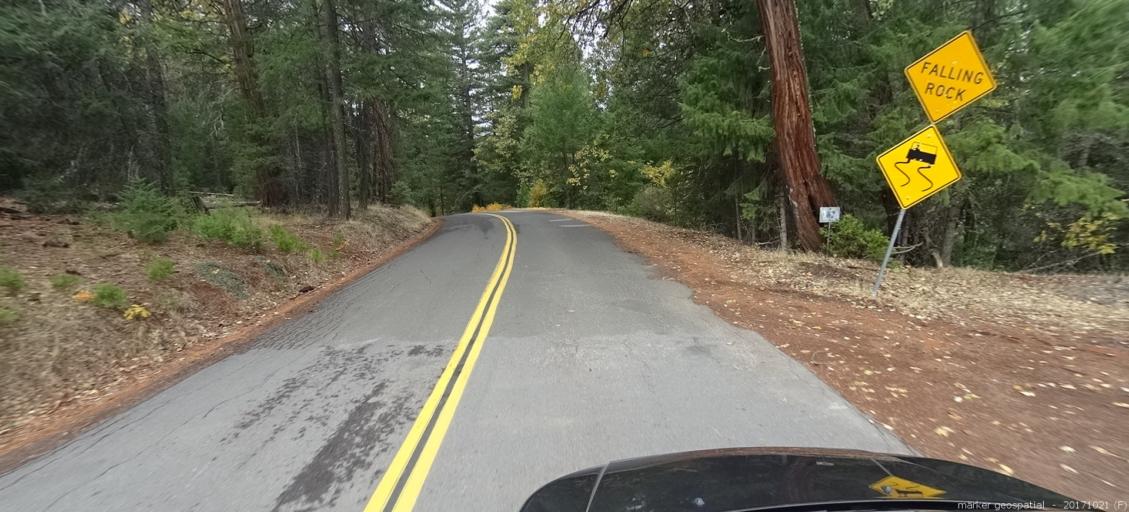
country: US
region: California
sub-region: Shasta County
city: Burney
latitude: 41.0194
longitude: -121.6662
